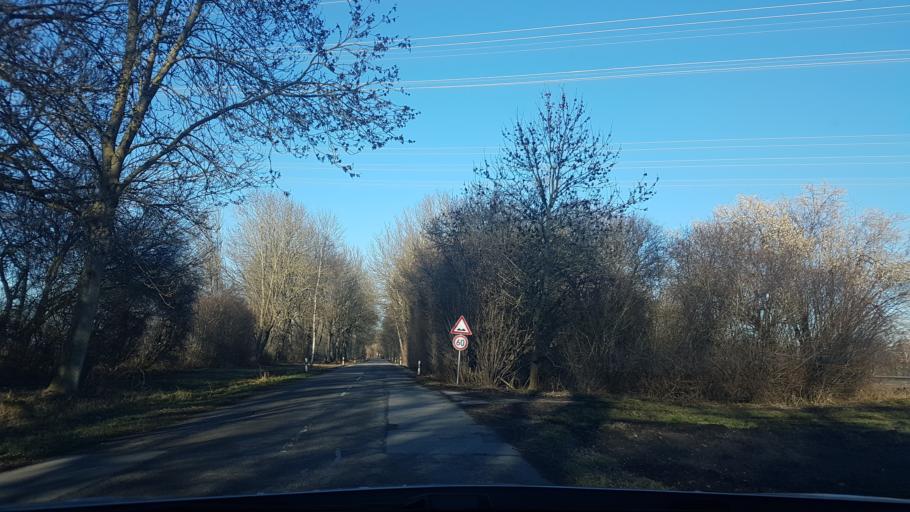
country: DE
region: Bavaria
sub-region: Upper Bavaria
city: Eichenried
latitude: 48.2779
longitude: 11.7517
